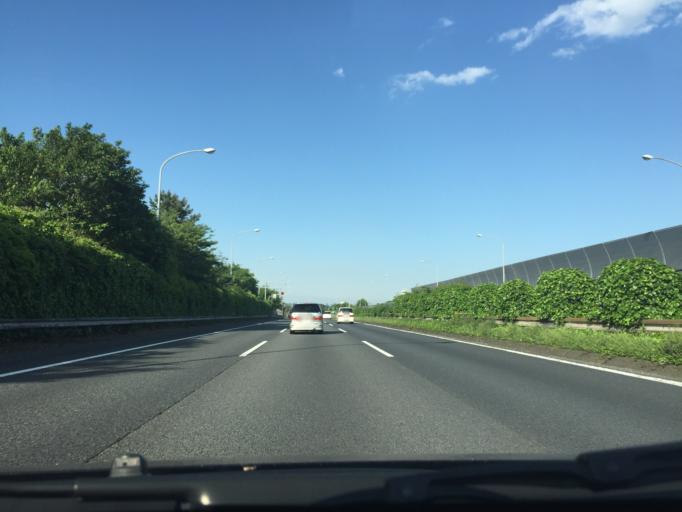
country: JP
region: Kanagawa
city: Minami-rinkan
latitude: 35.4838
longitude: 139.4616
